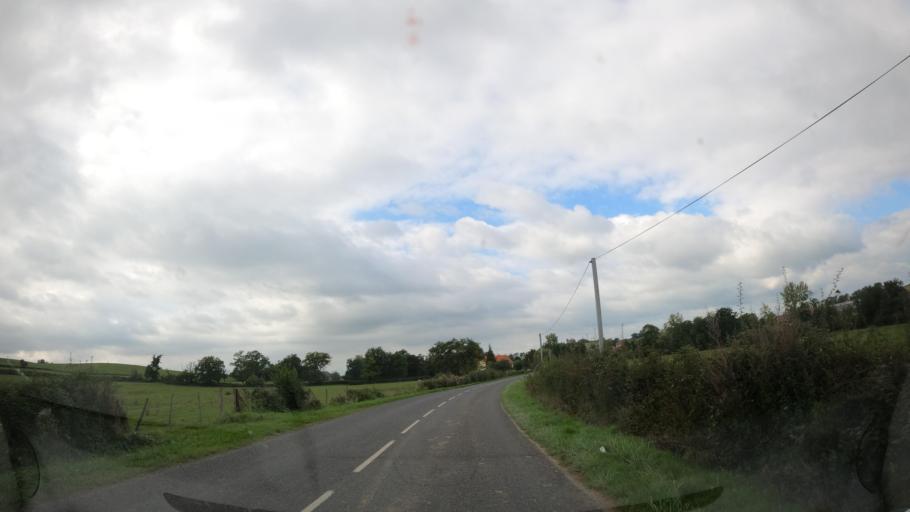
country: FR
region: Auvergne
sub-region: Departement de l'Allier
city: Lapalisse
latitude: 46.3212
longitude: 3.6325
